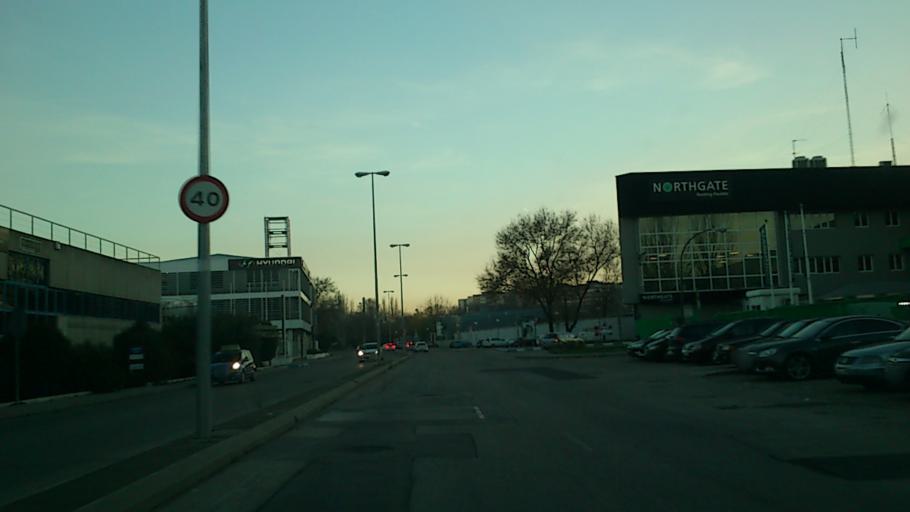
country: ES
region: Madrid
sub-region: Provincia de Madrid
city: San Fernando de Henares
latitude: 40.4361
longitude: -3.5409
